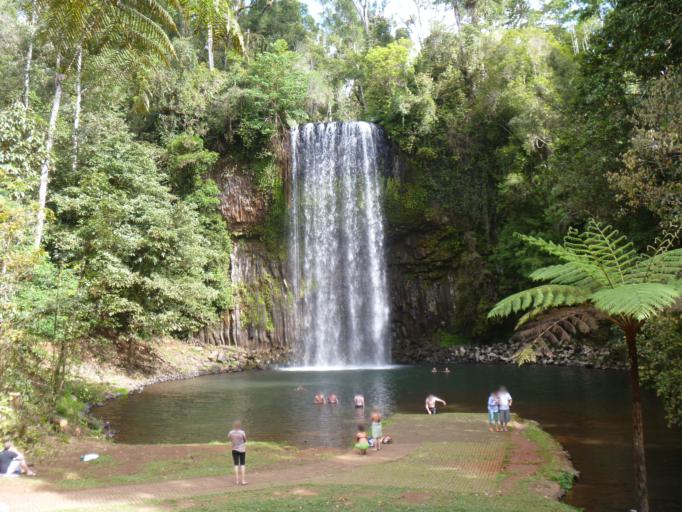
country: AU
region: Queensland
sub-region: Tablelands
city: Ravenshoe
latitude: -17.4952
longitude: 145.6108
